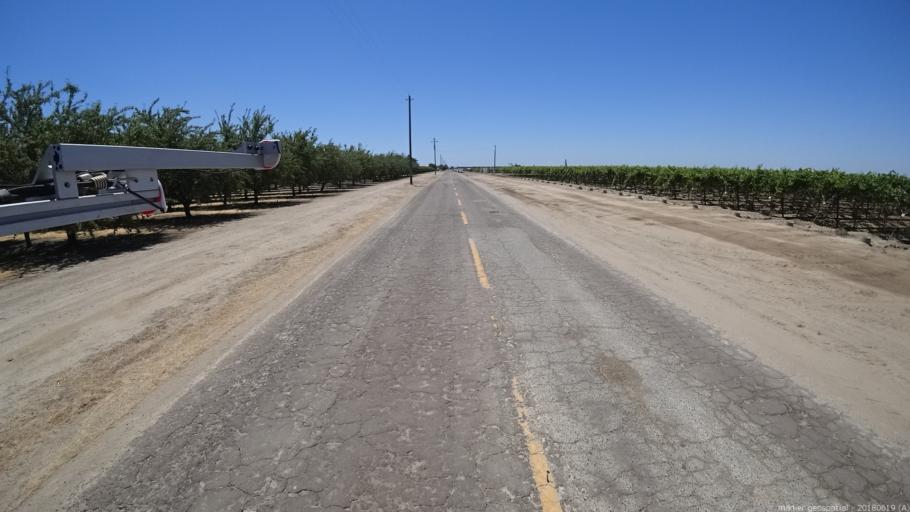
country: US
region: California
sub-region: Madera County
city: Parkwood
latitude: 36.8633
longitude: -120.0741
